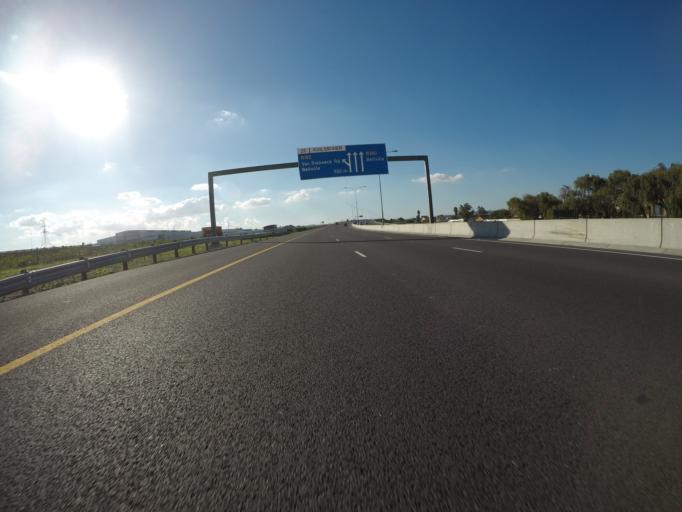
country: ZA
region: Western Cape
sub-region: City of Cape Town
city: Kraaifontein
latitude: -33.9236
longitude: 18.6635
